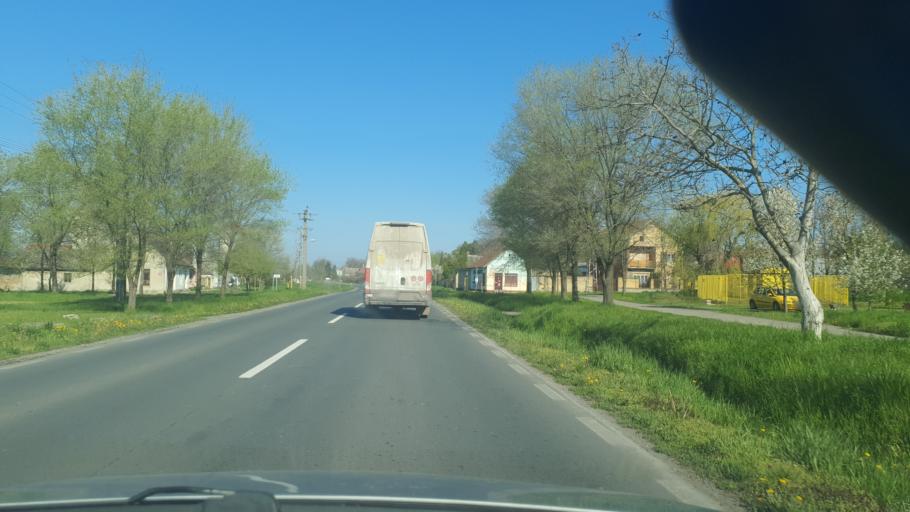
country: RS
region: Autonomna Pokrajina Vojvodina
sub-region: Zapadnobacki Okrug
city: Kula
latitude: 45.6891
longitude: 19.3882
